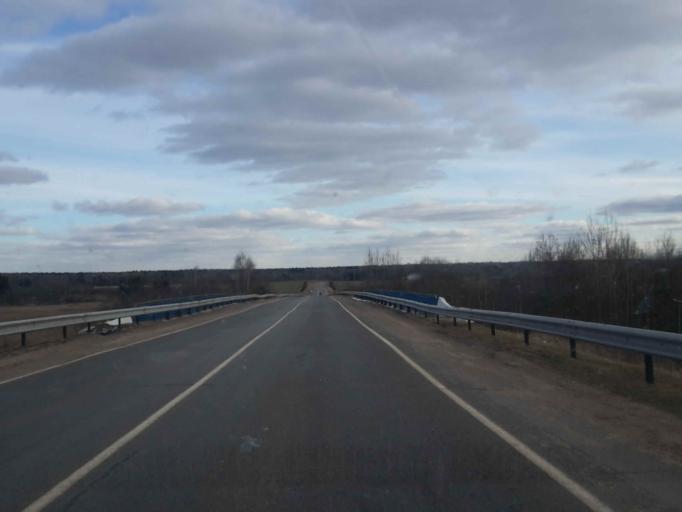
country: BY
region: Minsk
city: Kryvichy
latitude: 54.6667
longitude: 27.1639
